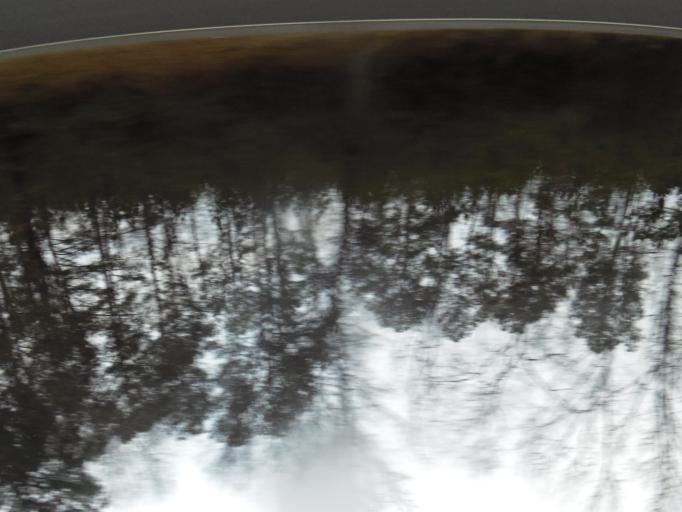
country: US
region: Alabama
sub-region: Blount County
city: Smoke Rise
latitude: 33.9437
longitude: -86.8697
